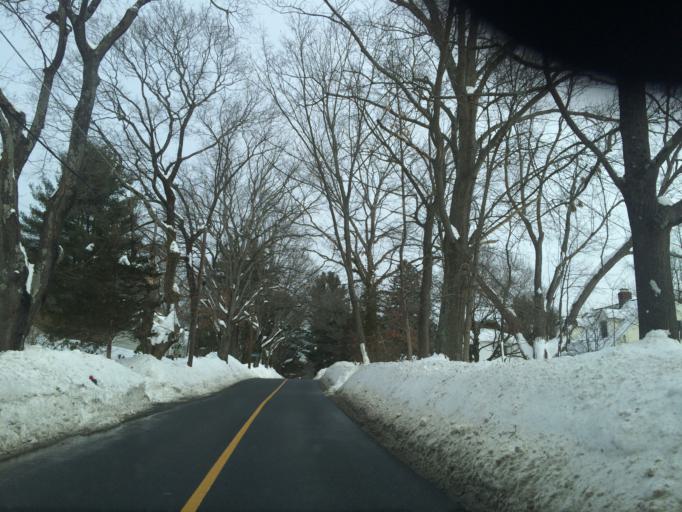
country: US
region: Massachusetts
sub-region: Middlesex County
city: Weston
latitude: 42.3908
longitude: -71.2961
